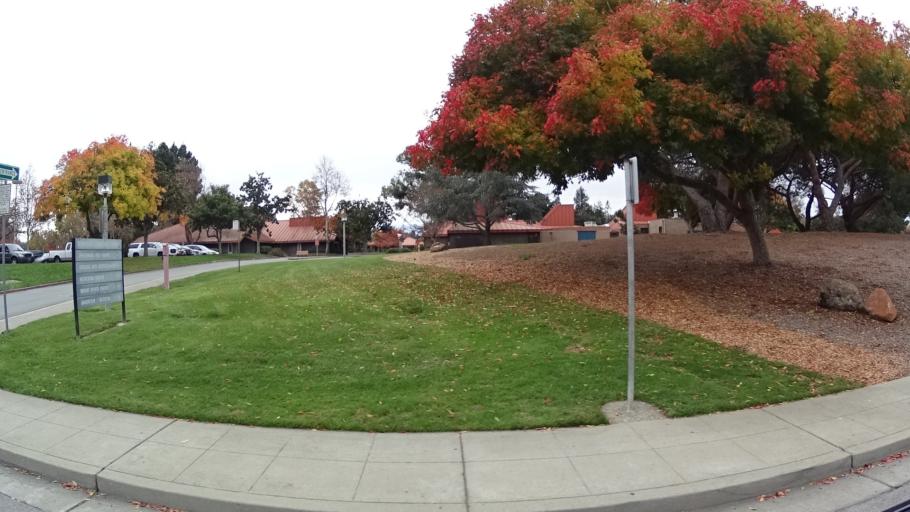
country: US
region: California
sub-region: Santa Clara County
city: Sunnyvale
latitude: 37.3591
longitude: -122.0244
